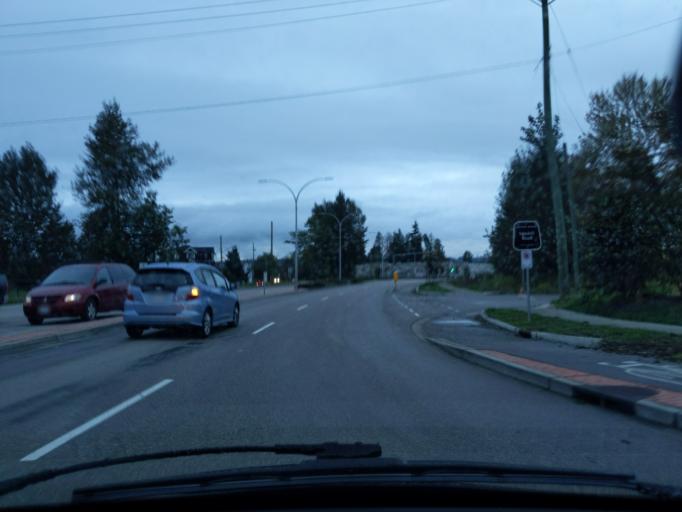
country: CA
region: British Columbia
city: New Westminster
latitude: 49.2067
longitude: -122.8673
